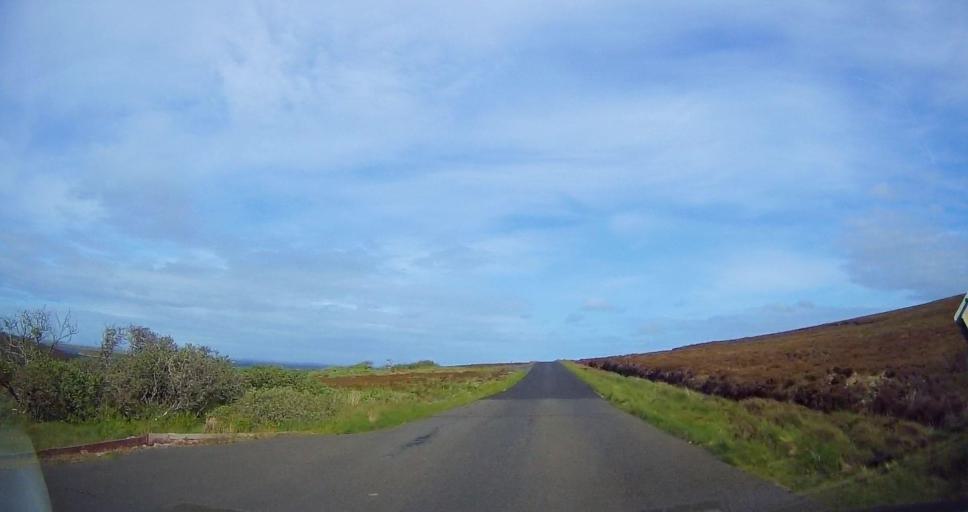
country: GB
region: Scotland
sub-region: Orkney Islands
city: Stromness
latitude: 58.8591
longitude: -3.2252
